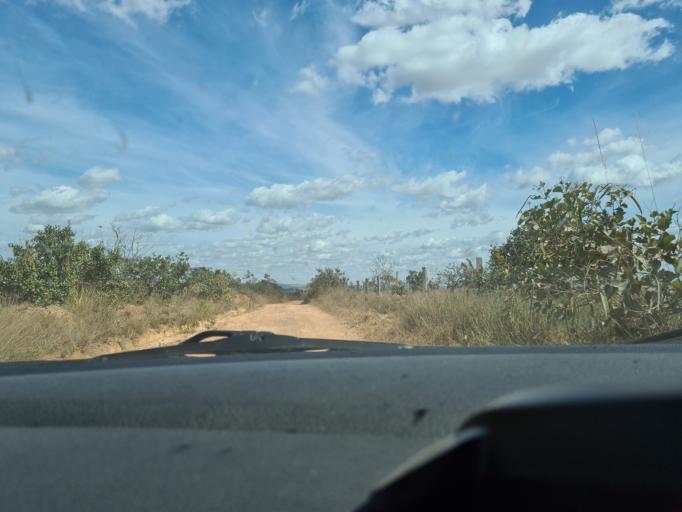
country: BR
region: Goias
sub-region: Silvania
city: Silvania
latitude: -16.5394
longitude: -48.5662
